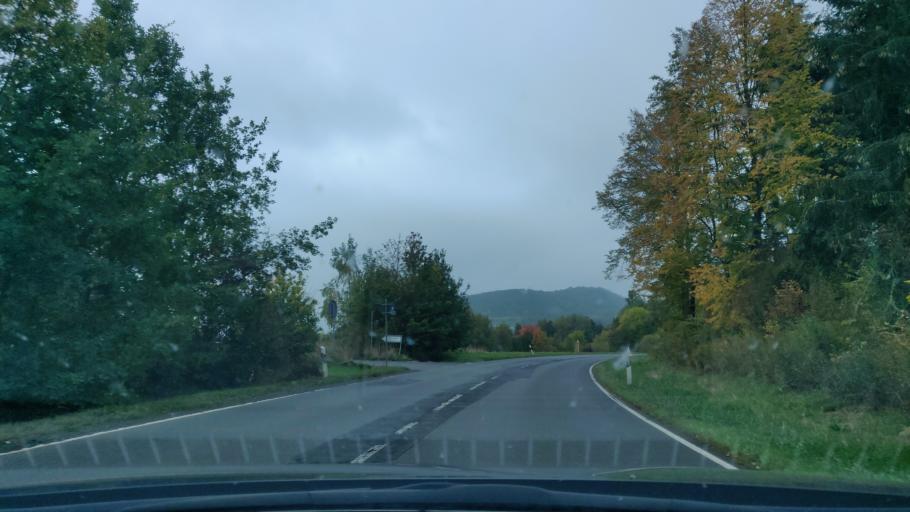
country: DE
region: Hesse
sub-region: Regierungsbezirk Kassel
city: Baunatal
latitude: 51.2509
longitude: 9.4229
